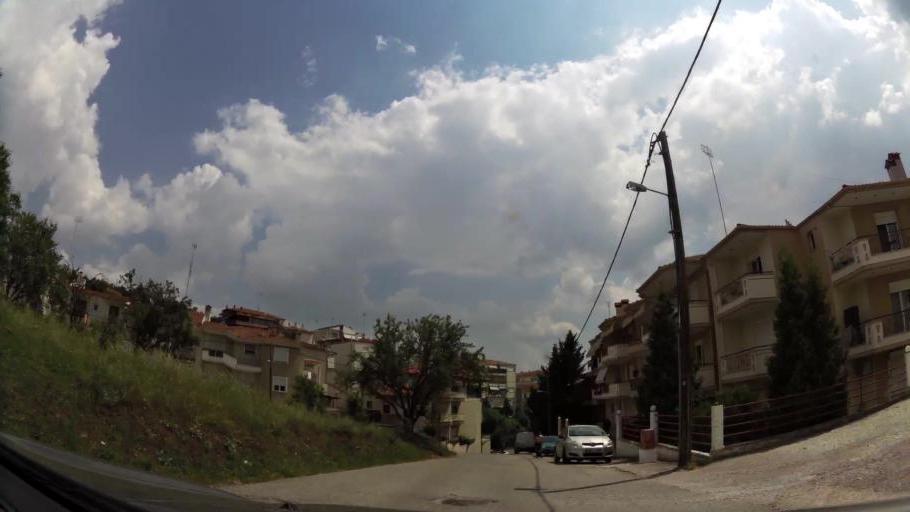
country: GR
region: West Macedonia
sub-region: Nomos Kozanis
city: Kozani
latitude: 40.3096
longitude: 21.7916
